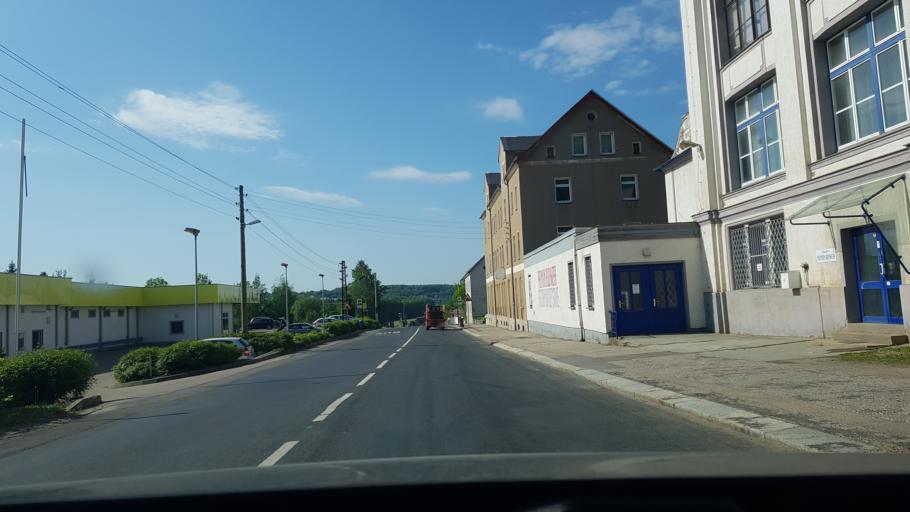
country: DE
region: Saxony
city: Wittgensdorf
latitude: 50.8759
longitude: 12.8709
